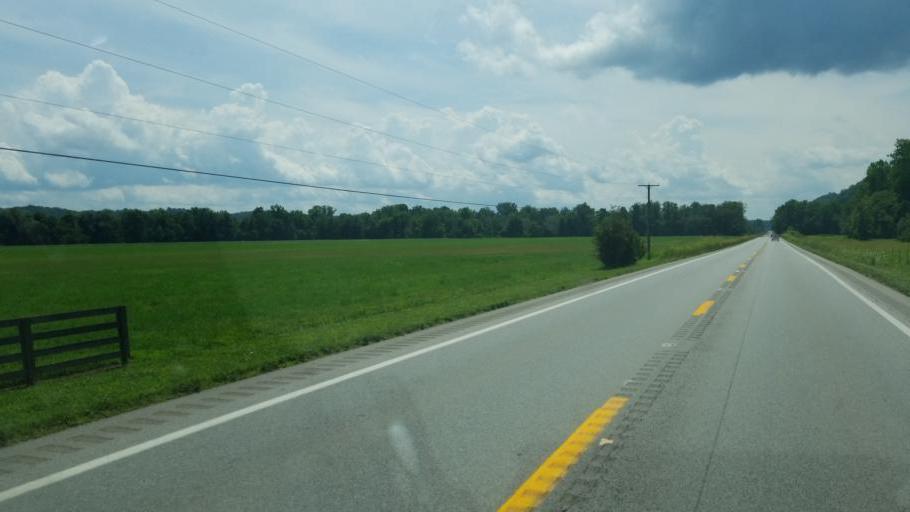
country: US
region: West Virginia
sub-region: Putnam County
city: Buffalo
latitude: 38.6293
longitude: -81.9805
